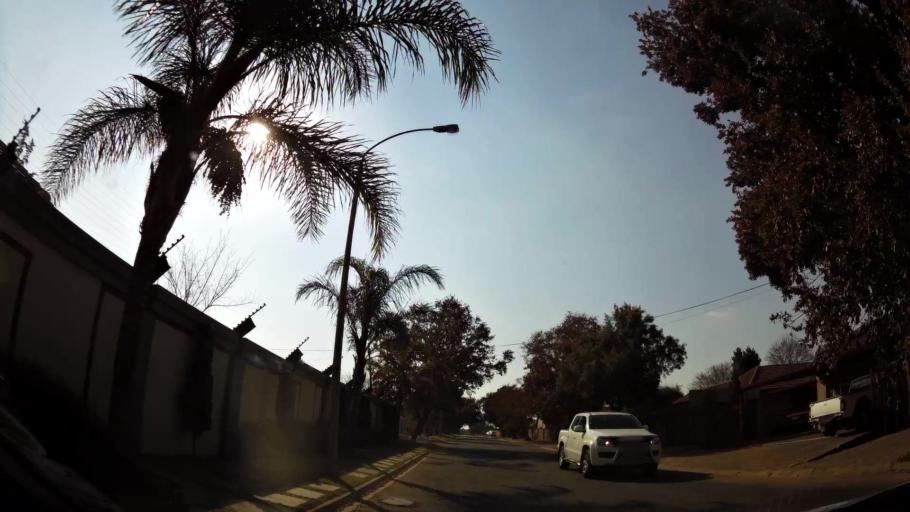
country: ZA
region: Gauteng
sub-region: Ekurhuleni Metropolitan Municipality
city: Boksburg
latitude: -26.1856
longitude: 28.2633
